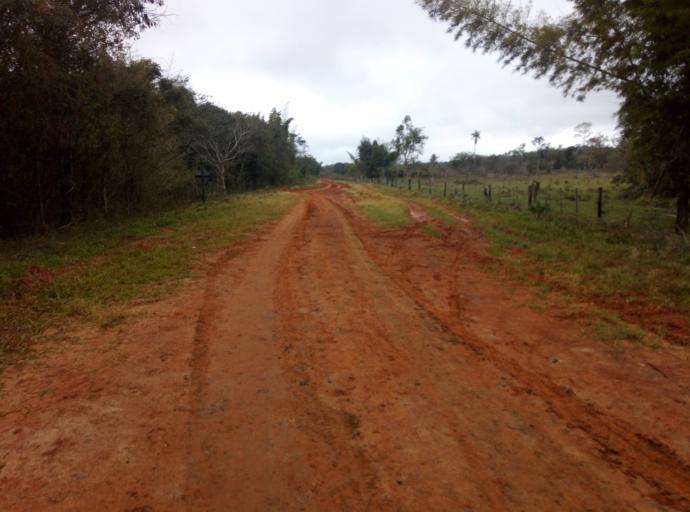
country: PY
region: Caaguazu
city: Doctor Cecilio Baez
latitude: -25.1205
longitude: -56.2151
